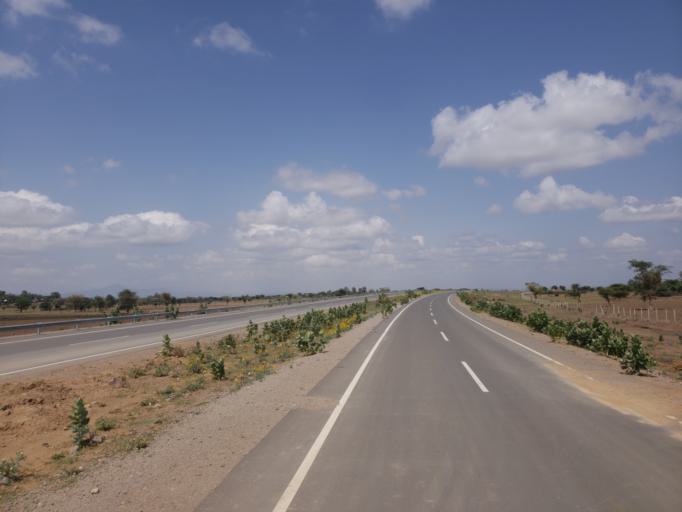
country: ET
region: Oromiya
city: Mojo
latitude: 8.5132
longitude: 39.0861
